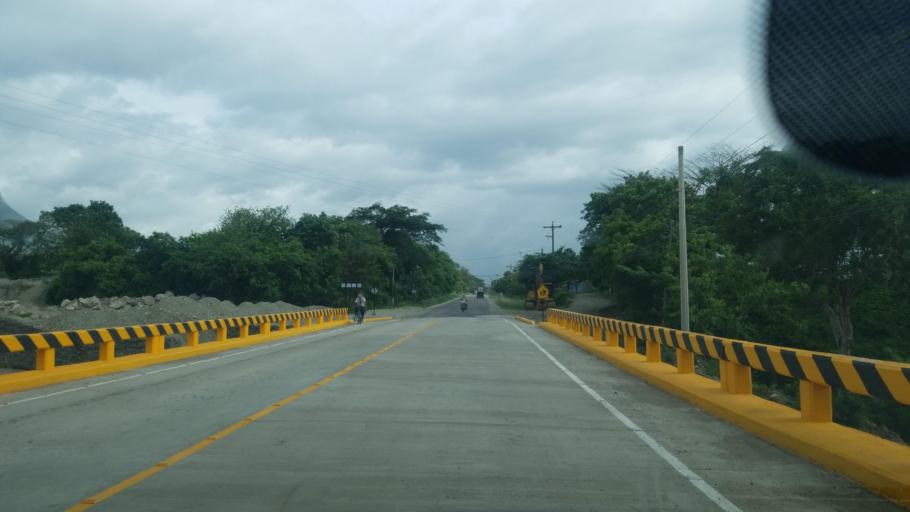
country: HN
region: Ocotepeque
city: Santa Lucia
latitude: 14.4136
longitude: -89.1946
